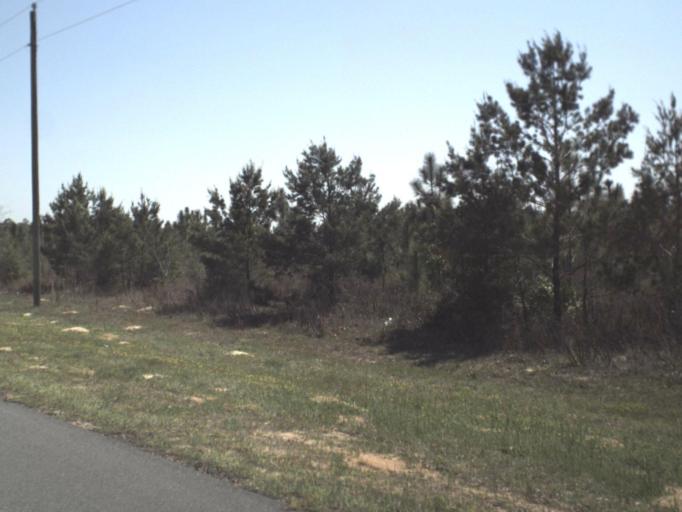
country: US
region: Florida
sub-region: Bay County
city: Youngstown
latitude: 30.4259
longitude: -85.3182
